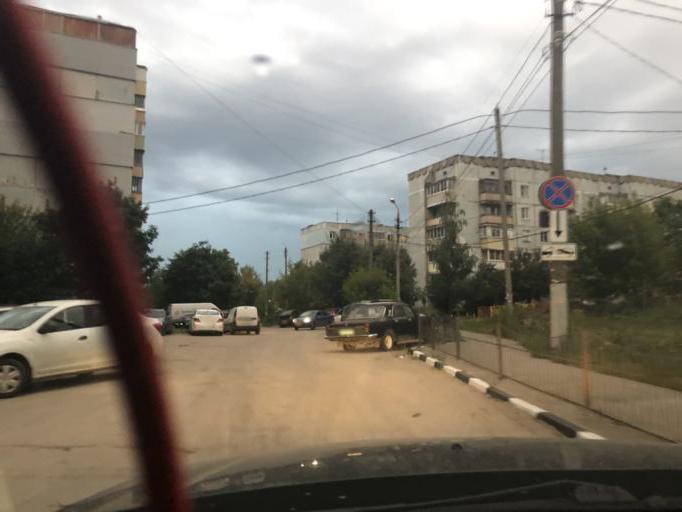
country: RU
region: Tula
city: Gorelki
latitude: 54.2269
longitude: 37.6159
